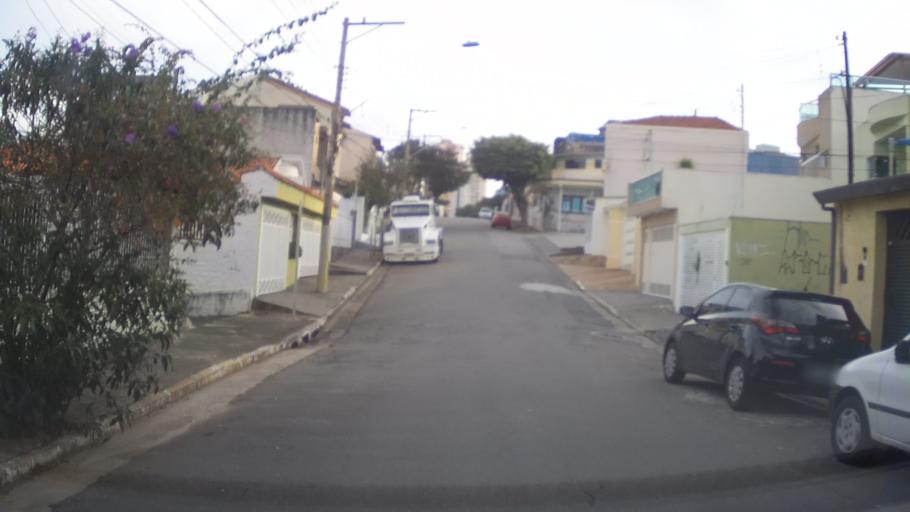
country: BR
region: Sao Paulo
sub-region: Sao Caetano Do Sul
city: Sao Caetano do Sul
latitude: -23.6267
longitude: -46.5621
